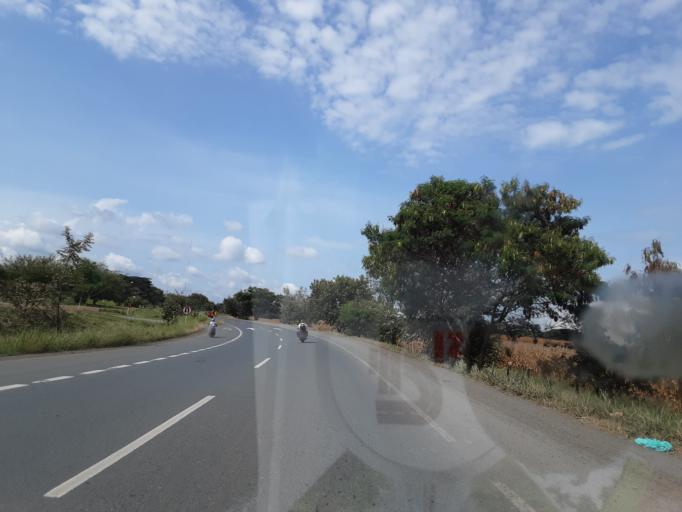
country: CO
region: Valle del Cauca
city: Guacari
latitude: 3.8105
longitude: -76.3086
